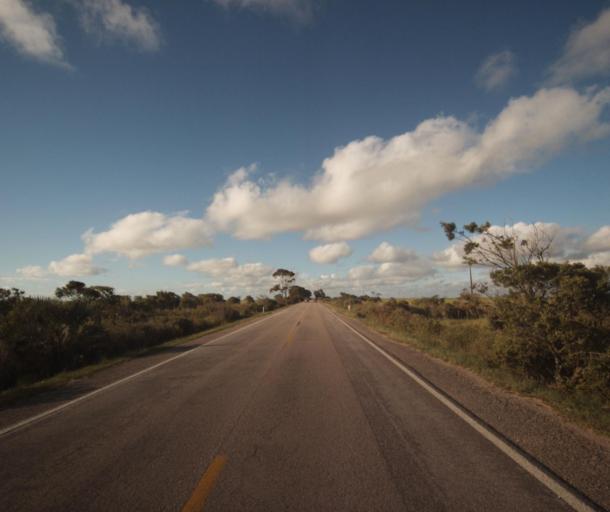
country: BR
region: Rio Grande do Sul
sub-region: Arroio Grande
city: Arroio Grande
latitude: -32.4855
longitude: -52.5791
